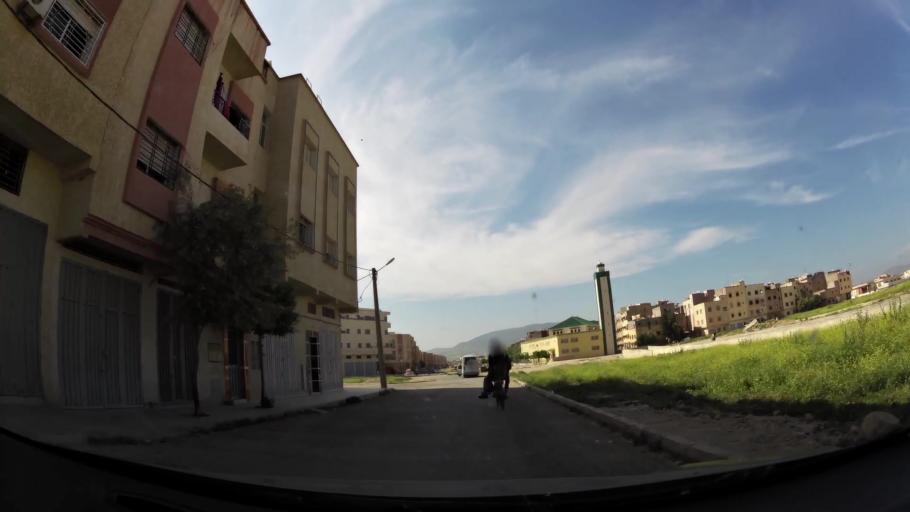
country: MA
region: Fes-Boulemane
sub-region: Fes
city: Fes
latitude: 34.0113
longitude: -5.0339
